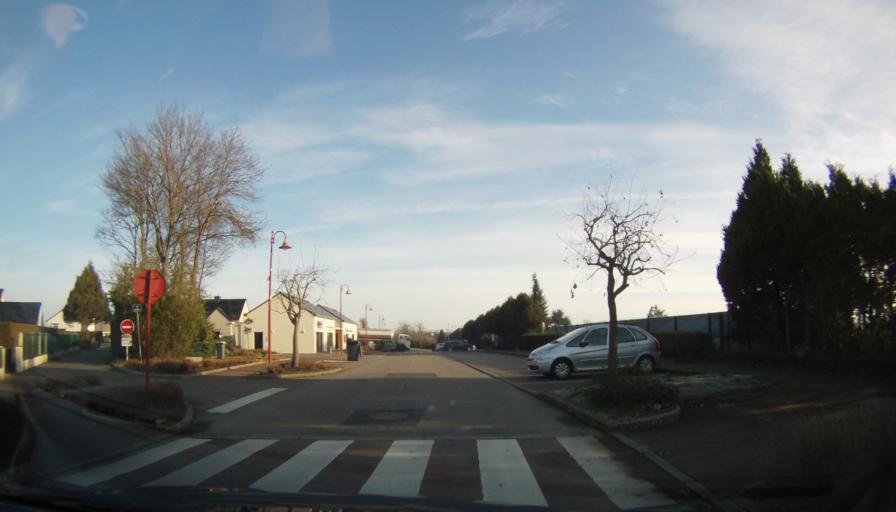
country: FR
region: Brittany
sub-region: Departement d'Ille-et-Vilaine
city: Bourgbarre
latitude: 47.9928
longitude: -1.6138
